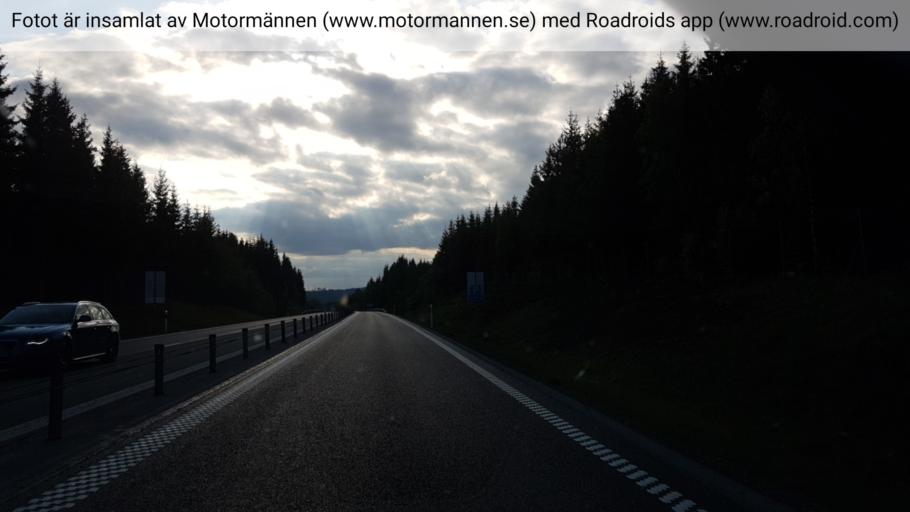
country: SE
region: Joenkoeping
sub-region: Jonkopings Kommun
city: Tenhult
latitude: 57.7156
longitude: 14.3959
